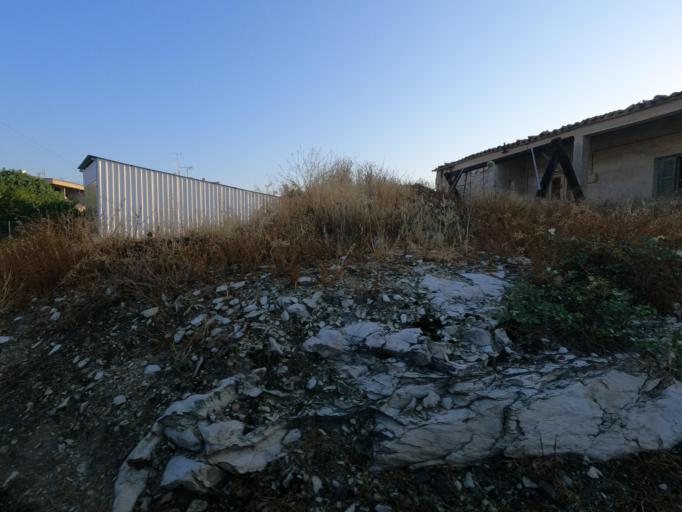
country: CY
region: Lefkosia
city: Alampra
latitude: 34.9883
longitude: 33.3997
